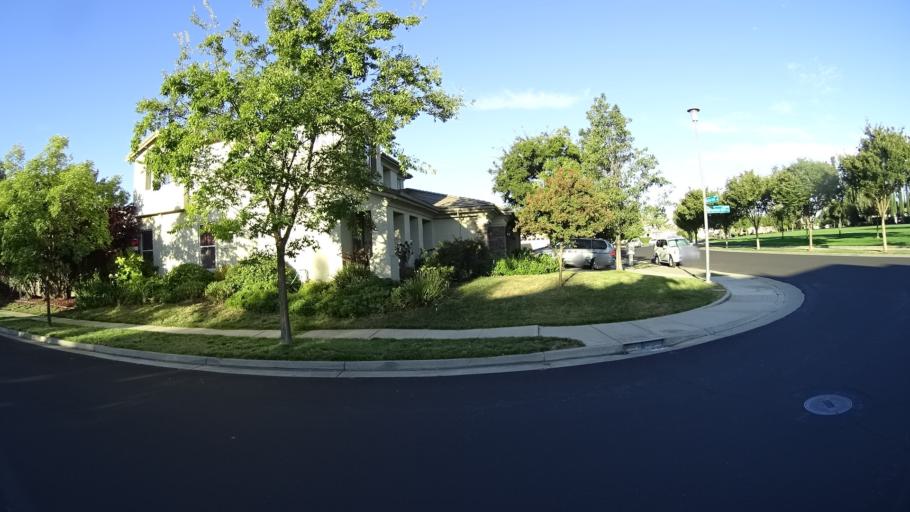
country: US
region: California
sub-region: Sacramento County
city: Laguna
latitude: 38.4018
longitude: -121.4721
